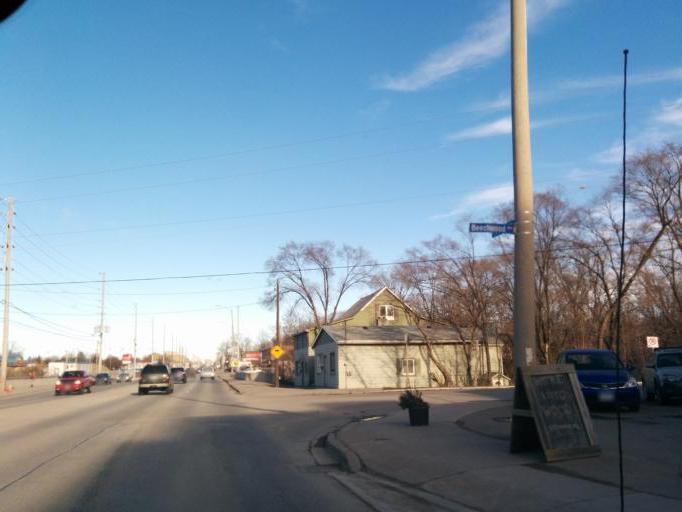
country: CA
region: Ontario
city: Etobicoke
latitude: 43.5662
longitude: -79.5700
